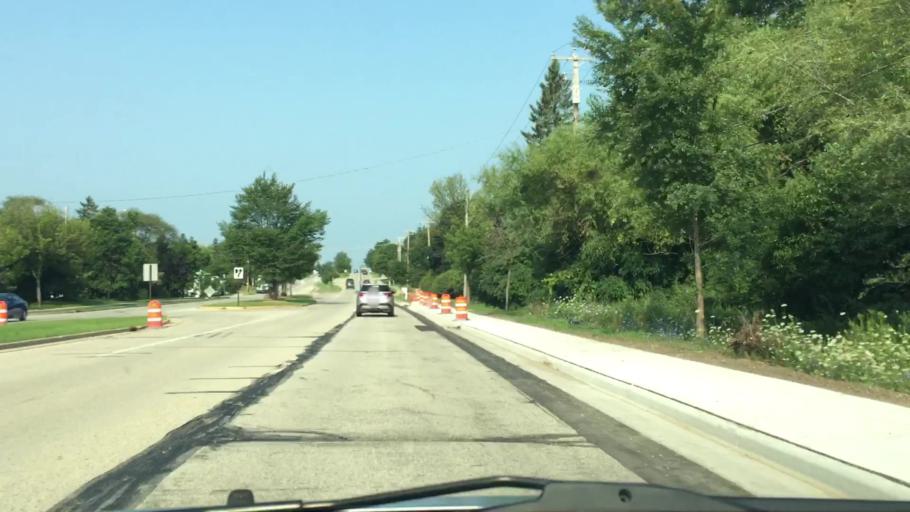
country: US
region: Wisconsin
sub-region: Waukesha County
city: New Berlin
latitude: 43.0168
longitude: -88.1151
